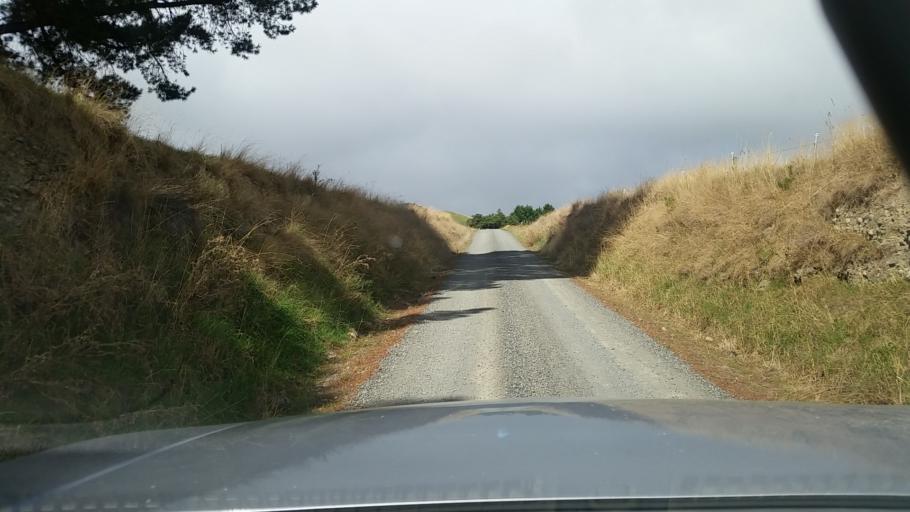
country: NZ
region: Marlborough
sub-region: Marlborough District
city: Blenheim
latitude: -41.7478
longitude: 173.8952
